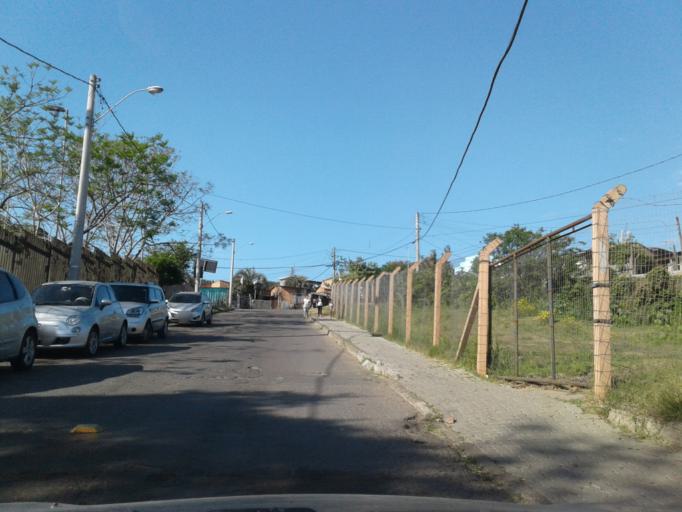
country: BR
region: Rio Grande do Sul
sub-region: Porto Alegre
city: Porto Alegre
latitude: -30.0482
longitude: -51.1555
